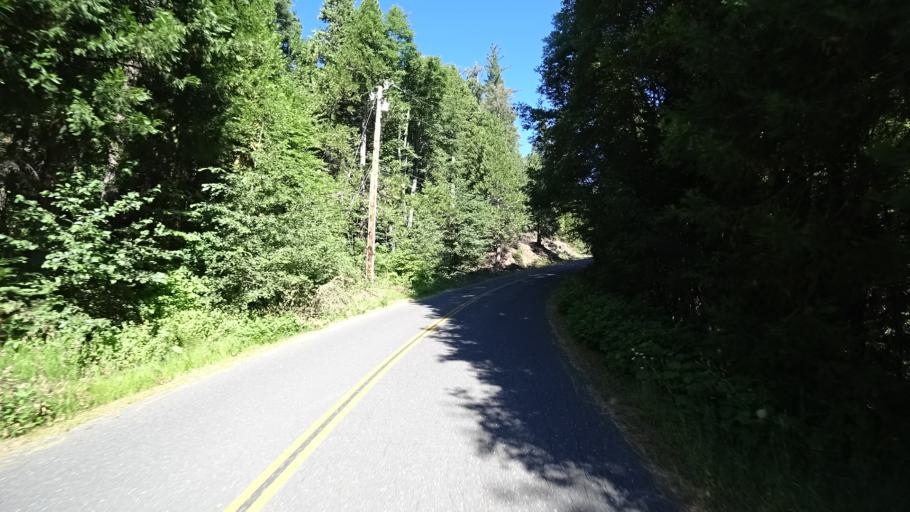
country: US
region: California
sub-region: Calaveras County
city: Arnold
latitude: 38.2864
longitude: -120.2726
